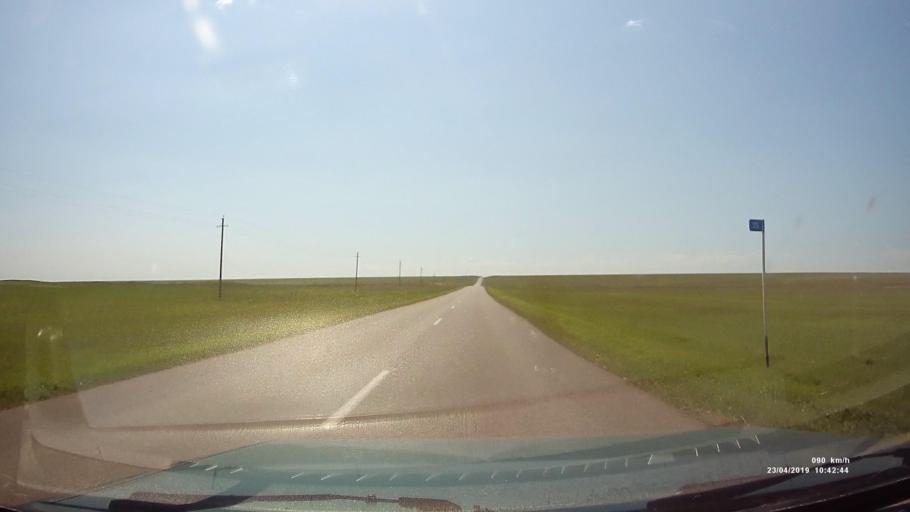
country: RU
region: Kalmykiya
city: Yashalta
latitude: 46.4787
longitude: 42.6466
